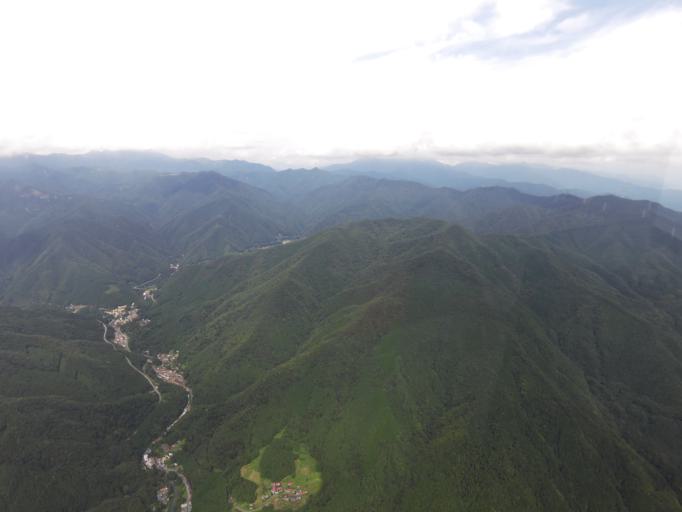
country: JP
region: Gunma
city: Nakanojomachi
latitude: 36.6663
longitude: 138.7905
